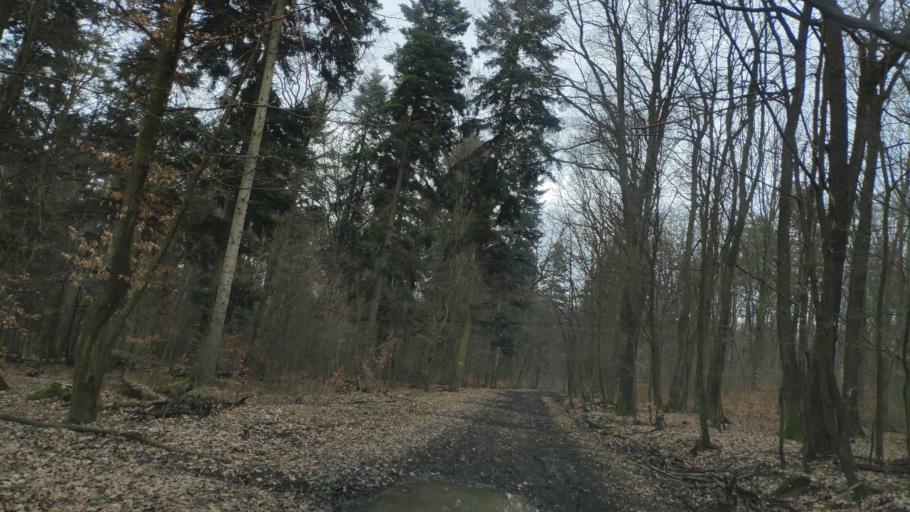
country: SK
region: Presovsky
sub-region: Okres Presov
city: Presov
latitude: 49.0729
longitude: 21.2778
